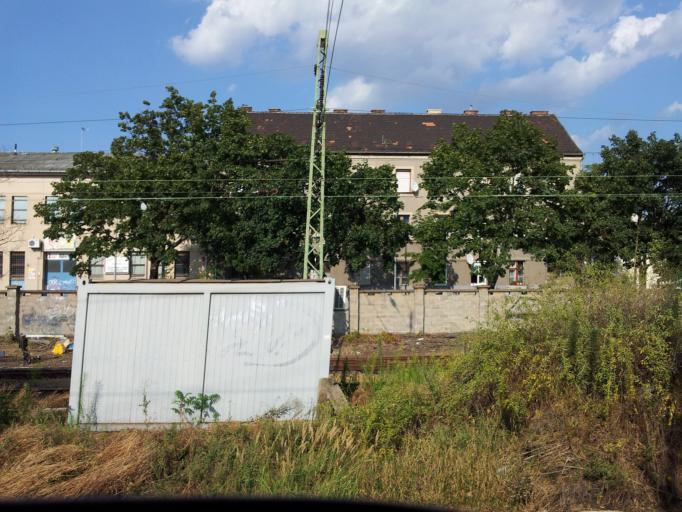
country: HU
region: Budapest
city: Budapest XIV. keruelet
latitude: 47.4885
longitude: 19.1232
